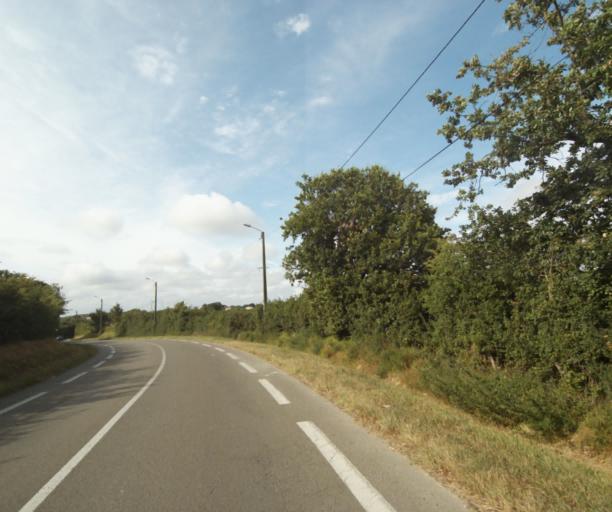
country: FR
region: Pays de la Loire
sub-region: Departement de la Vendee
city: Chateau-d'Olonne
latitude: 46.4968
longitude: -1.7331
